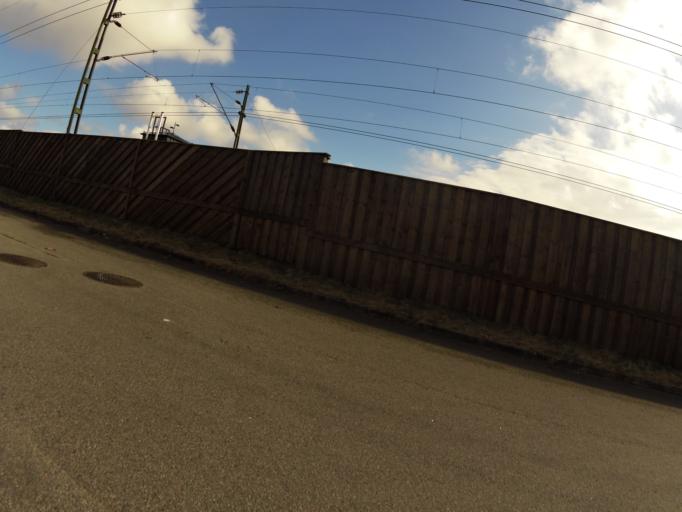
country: SE
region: Halland
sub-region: Halmstads Kommun
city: Halmstad
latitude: 56.6795
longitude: 12.8745
